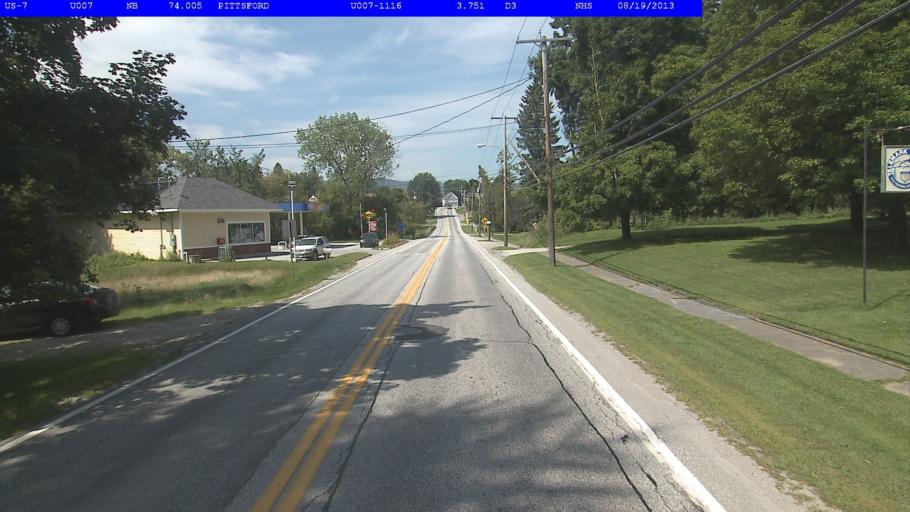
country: US
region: Vermont
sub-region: Rutland County
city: Rutland
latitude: 43.7066
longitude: -73.0237
